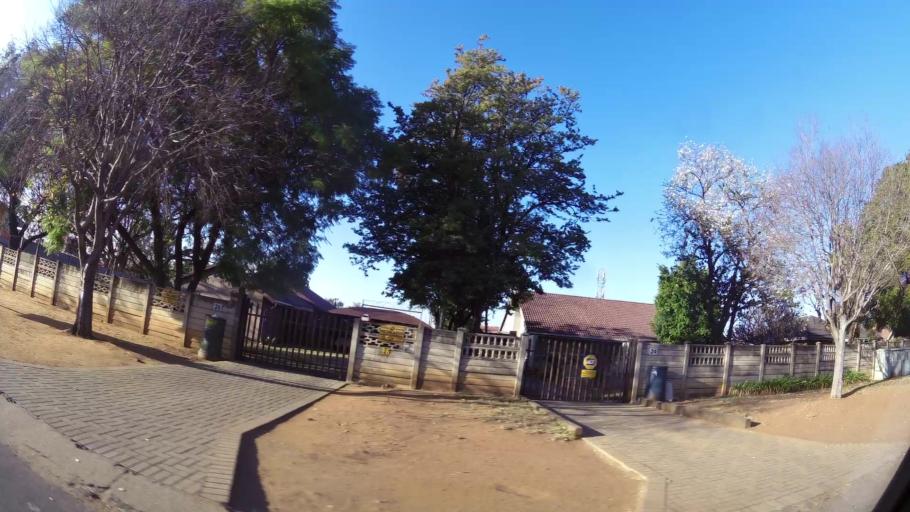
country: ZA
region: North-West
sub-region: Bojanala Platinum District Municipality
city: Rustenburg
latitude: -25.6806
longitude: 27.2165
